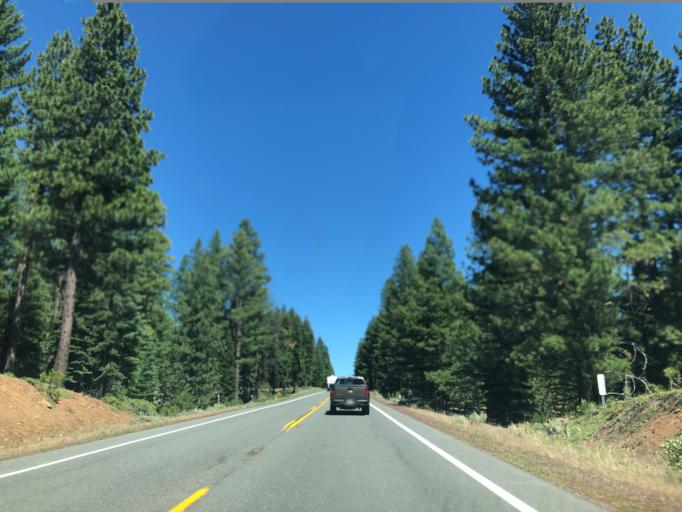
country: US
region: California
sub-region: Lassen County
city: Susanville
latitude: 40.4392
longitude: -120.8473
